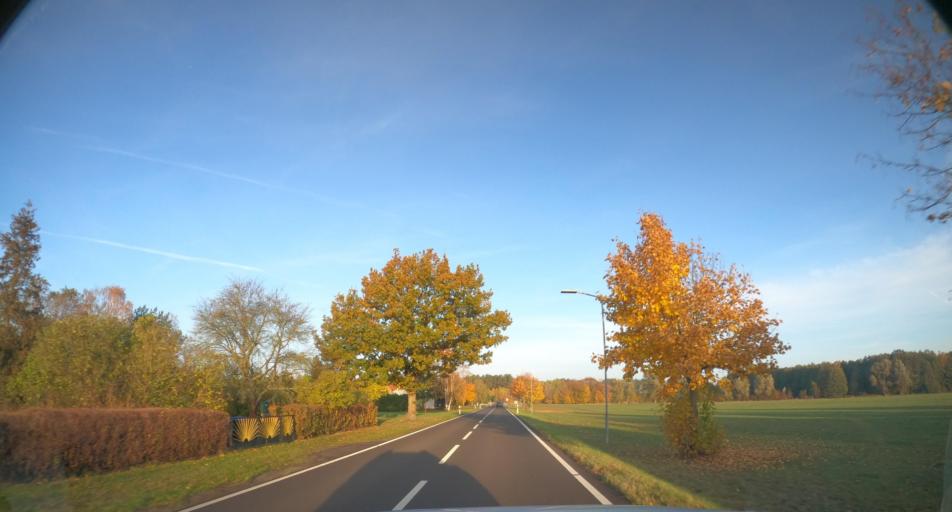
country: DE
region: Mecklenburg-Vorpommern
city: Ahlbeck
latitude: 53.6456
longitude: 14.1971
